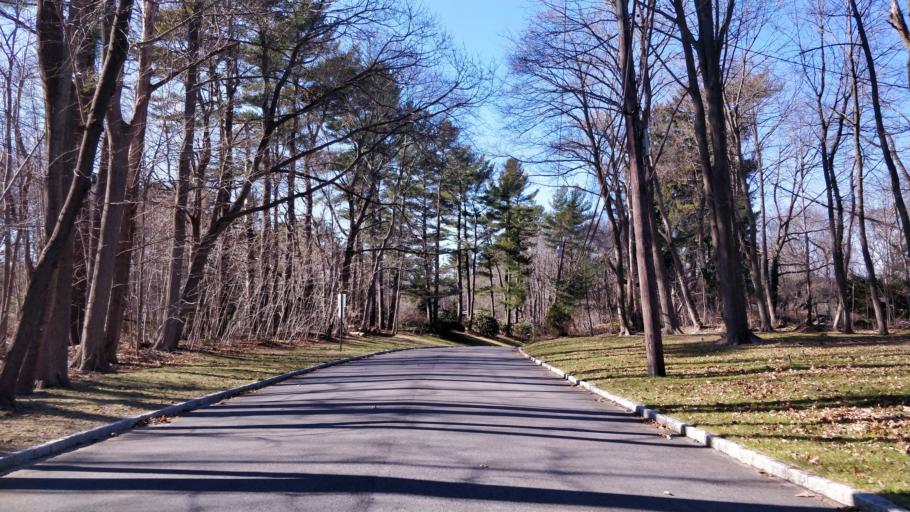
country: US
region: New York
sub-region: Nassau County
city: East Norwich
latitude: 40.8504
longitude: -73.5404
